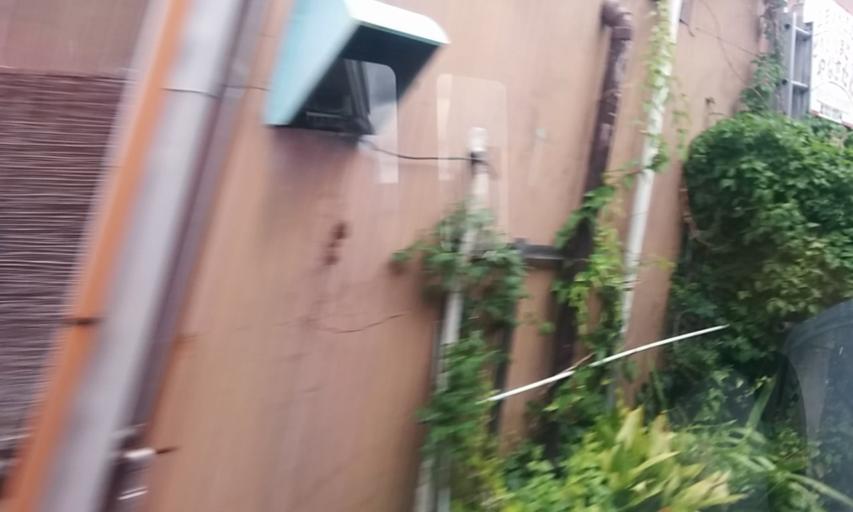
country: JP
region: Osaka
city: Mino
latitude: 34.8187
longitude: 135.4651
